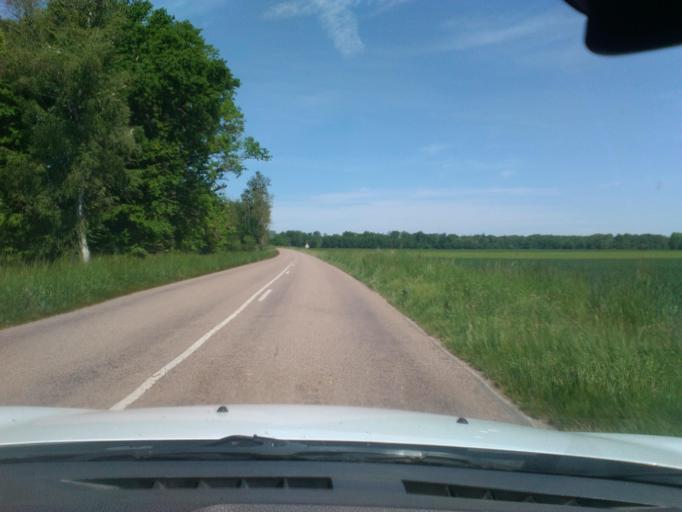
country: FR
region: Lorraine
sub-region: Departement des Vosges
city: Rambervillers
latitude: 48.4150
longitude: 6.5862
